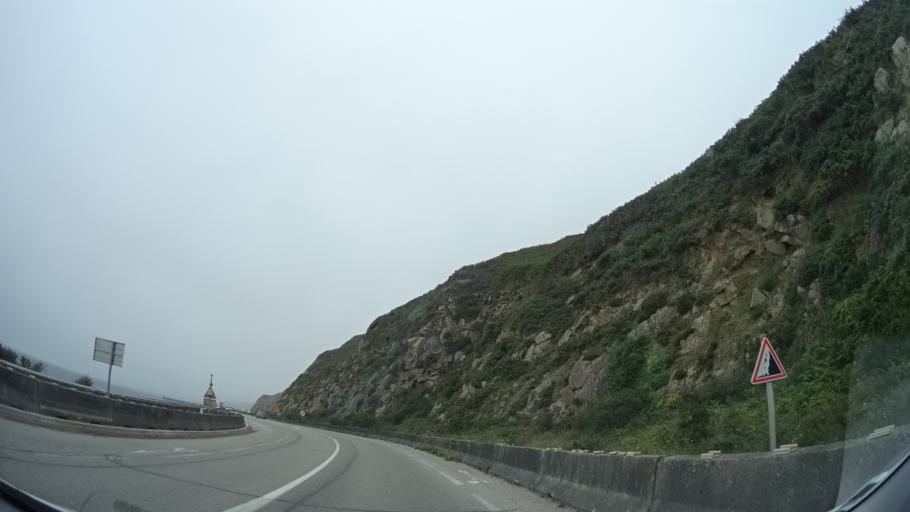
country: FR
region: Lower Normandy
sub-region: Departement de la Manche
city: Flamanville
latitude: 49.5454
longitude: -1.8726
